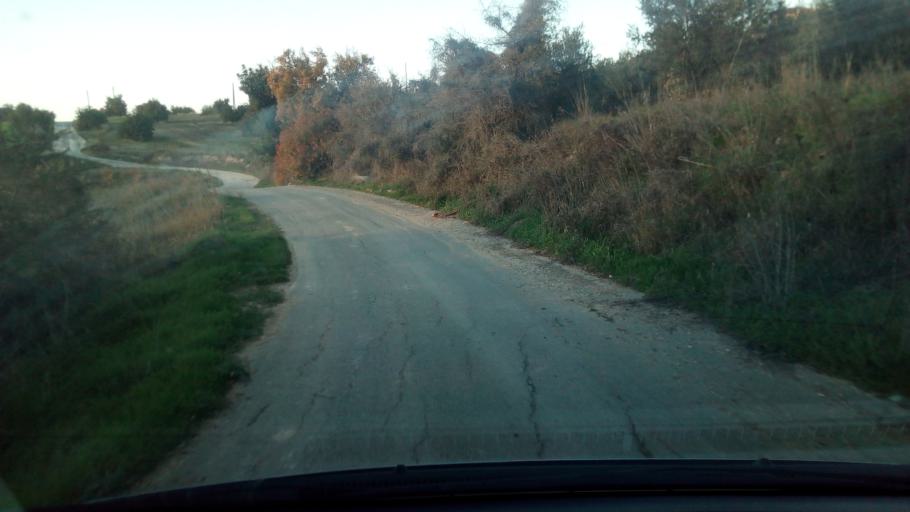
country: CY
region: Pafos
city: Polis
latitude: 34.9837
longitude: 32.4789
